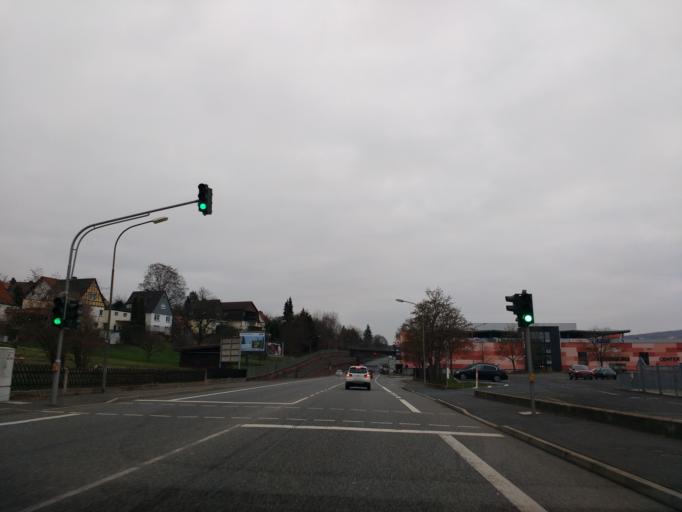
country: DE
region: Hesse
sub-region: Regierungsbezirk Kassel
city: Rotenburg an der Fulda
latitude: 51.0012
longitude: 9.7302
